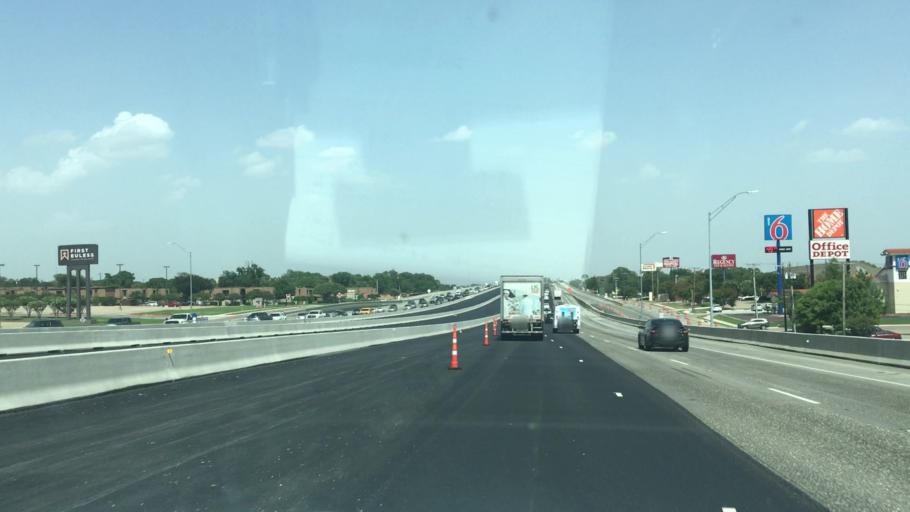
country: US
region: Texas
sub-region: Tarrant County
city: Euless
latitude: 32.8375
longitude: -97.0993
